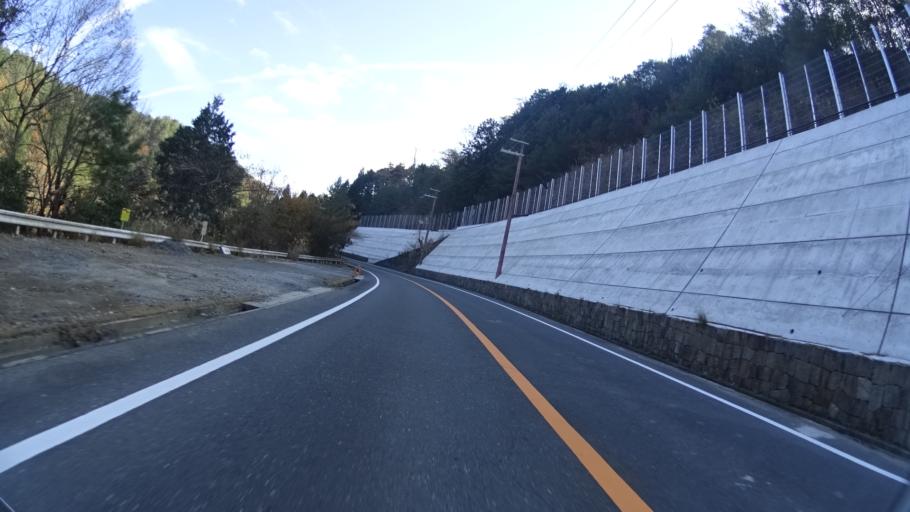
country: JP
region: Kyoto
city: Kameoka
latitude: 35.1350
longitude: 135.5352
